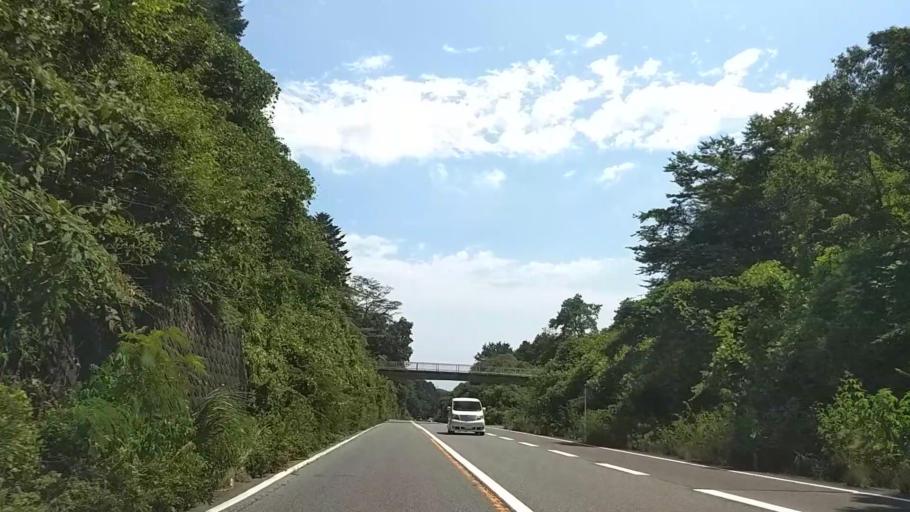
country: JP
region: Shizuoka
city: Fujinomiya
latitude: 35.2912
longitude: 138.6087
